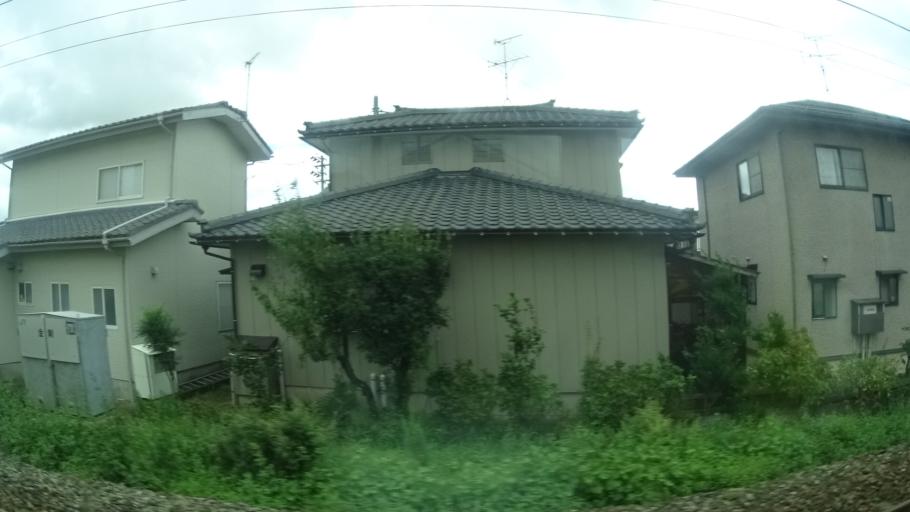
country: JP
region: Niigata
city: Shibata
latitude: 37.9538
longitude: 139.3439
